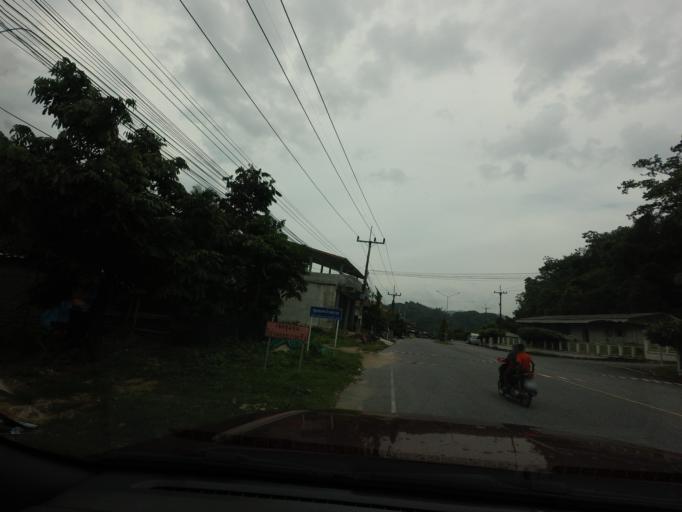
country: TH
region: Yala
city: Than To
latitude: 6.1614
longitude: 101.2710
